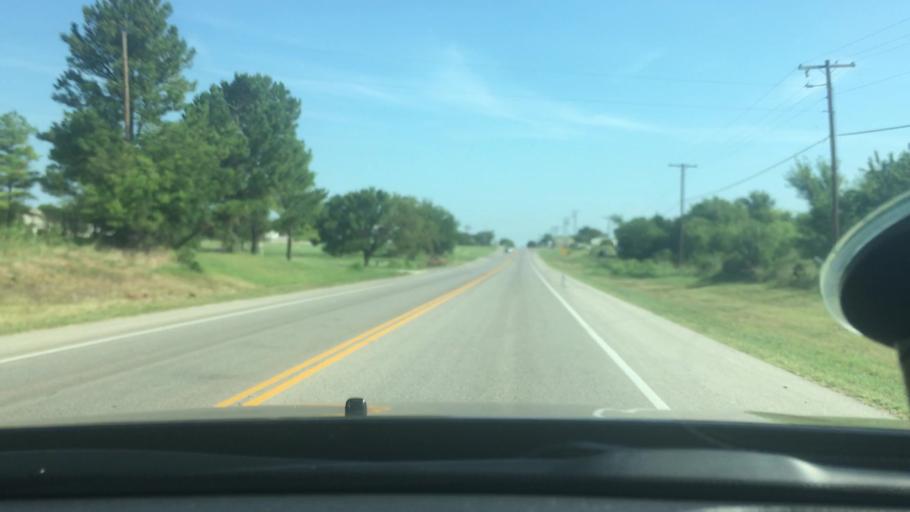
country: US
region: Oklahoma
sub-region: Garvin County
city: Pauls Valley
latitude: 34.7022
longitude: -97.2128
